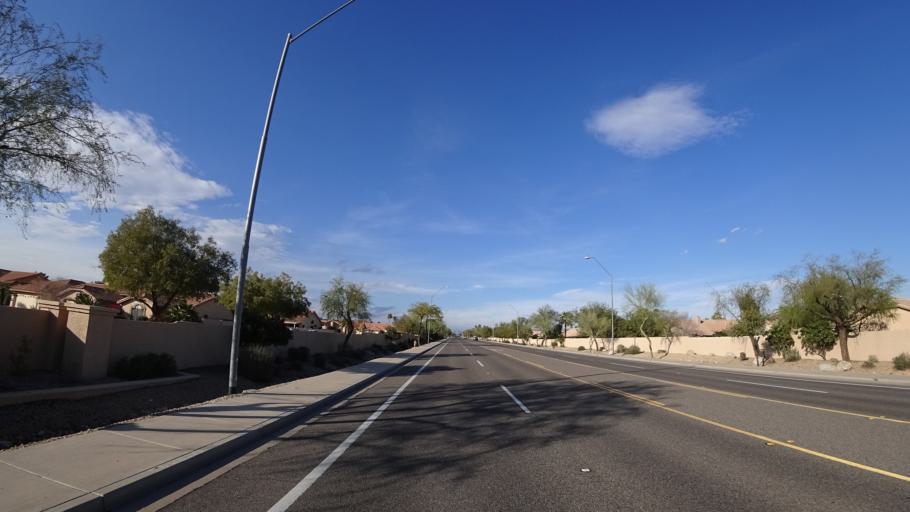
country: US
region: Arizona
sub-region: Maricopa County
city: Sun City
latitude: 33.6602
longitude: -112.2551
